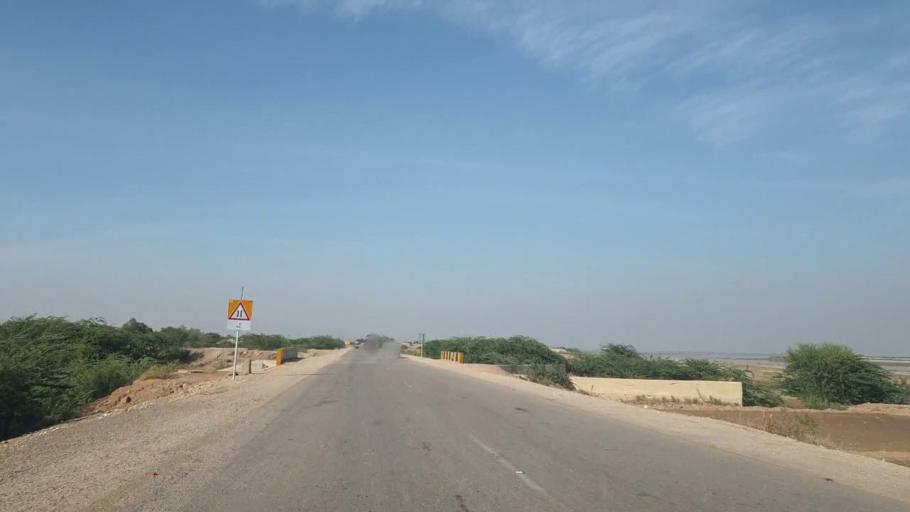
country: PK
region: Sindh
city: Sehwan
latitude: 26.3792
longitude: 67.8724
